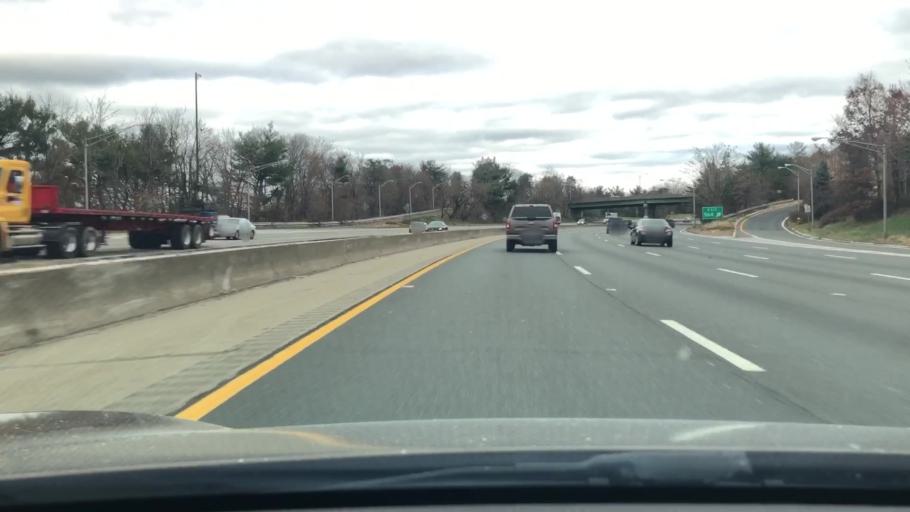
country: US
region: New Jersey
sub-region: Passaic County
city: Woodland Park
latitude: 40.9024
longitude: -74.1956
